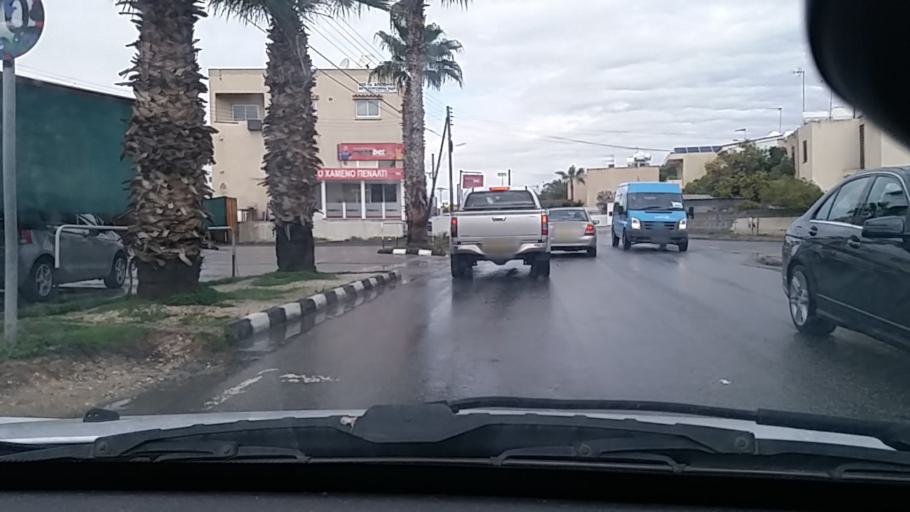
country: CY
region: Larnaka
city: Larnaca
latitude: 34.9330
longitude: 33.6223
